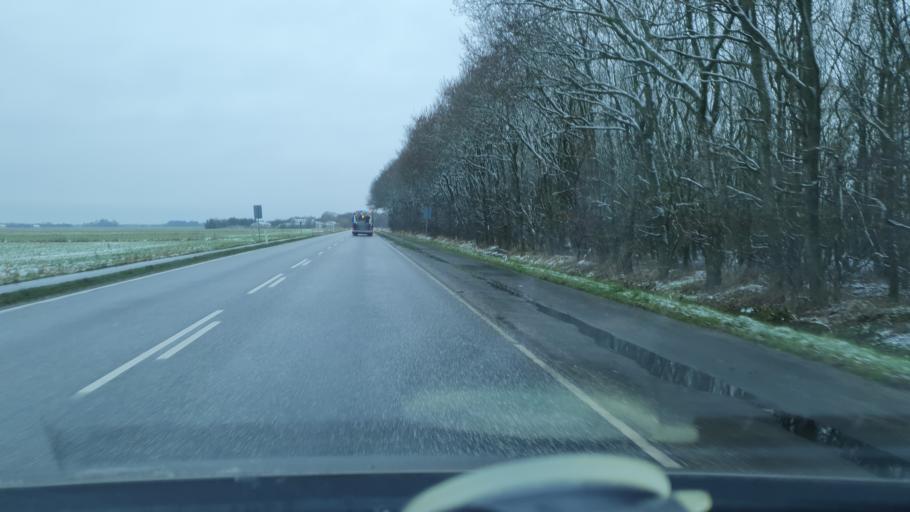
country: DK
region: North Denmark
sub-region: Jammerbugt Kommune
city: Brovst
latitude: 57.1201
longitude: 9.6171
